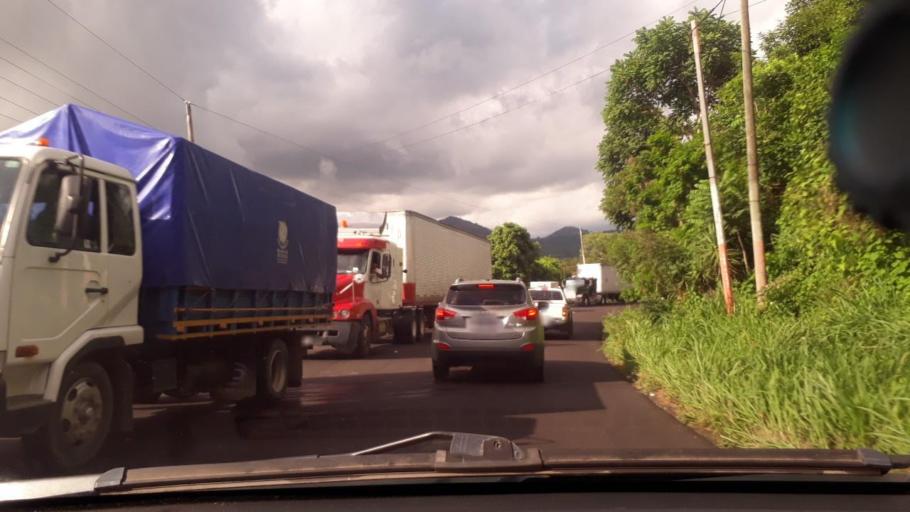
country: GT
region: Jutiapa
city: Quesada
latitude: 14.2704
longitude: -90.0082
